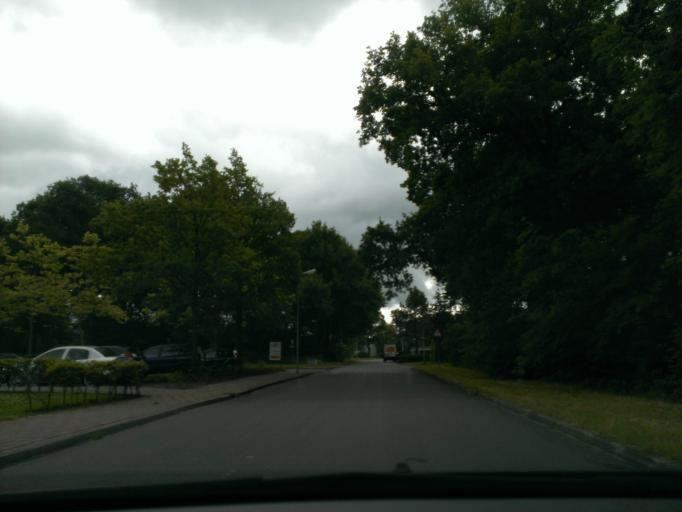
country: NL
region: Drenthe
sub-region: Gemeente Hoogeveen
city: Hoogeveen
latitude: 52.7351
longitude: 6.4995
